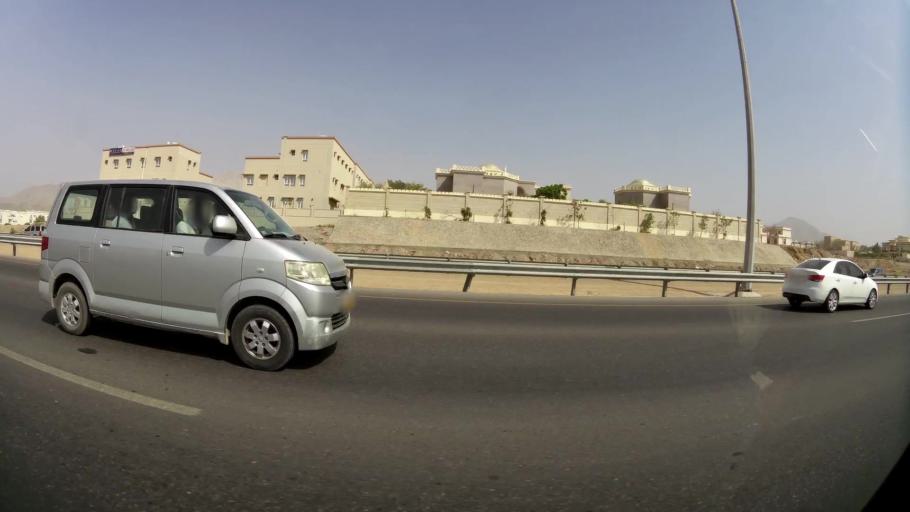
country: OM
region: Muhafazat Masqat
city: Bawshar
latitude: 23.5674
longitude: 58.3977
